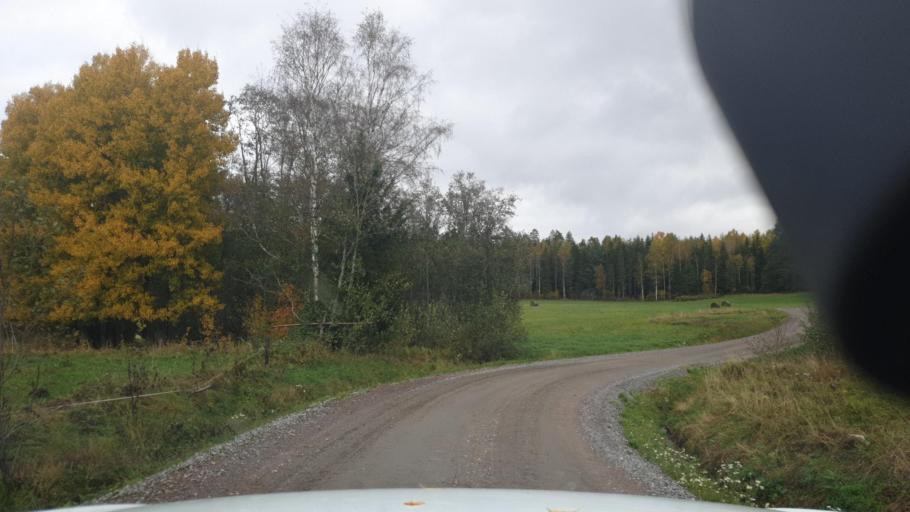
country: SE
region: Vaermland
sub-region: Karlstads Kommun
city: Edsvalla
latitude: 59.4793
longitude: 13.1327
